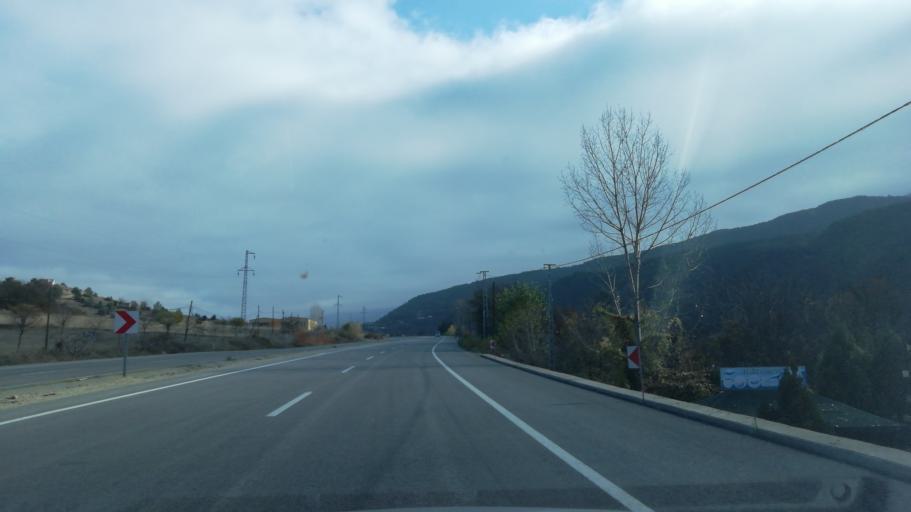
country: TR
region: Karabuk
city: Safranbolu
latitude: 41.2177
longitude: 32.7484
